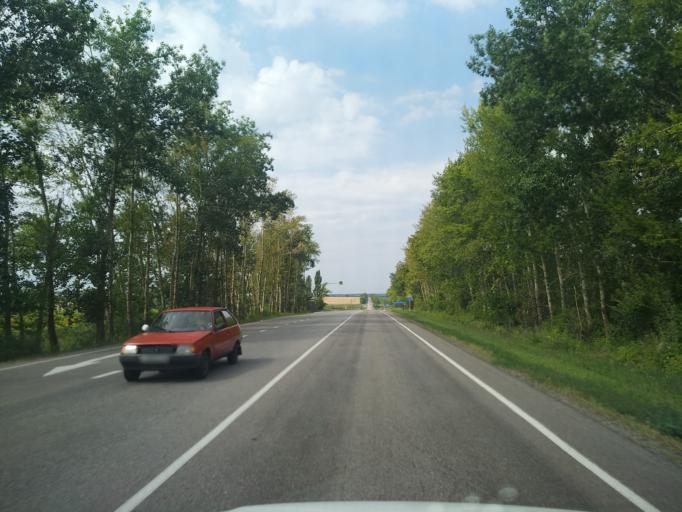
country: RU
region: Voronezj
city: Verkhnyaya Khava
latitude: 51.7045
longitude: 39.9800
